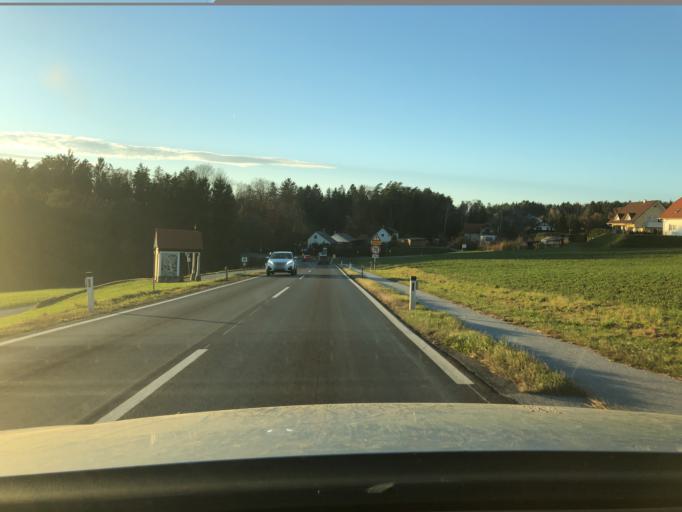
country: AT
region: Styria
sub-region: Politischer Bezirk Weiz
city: Nitscha
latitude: 47.1034
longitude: 15.7416
